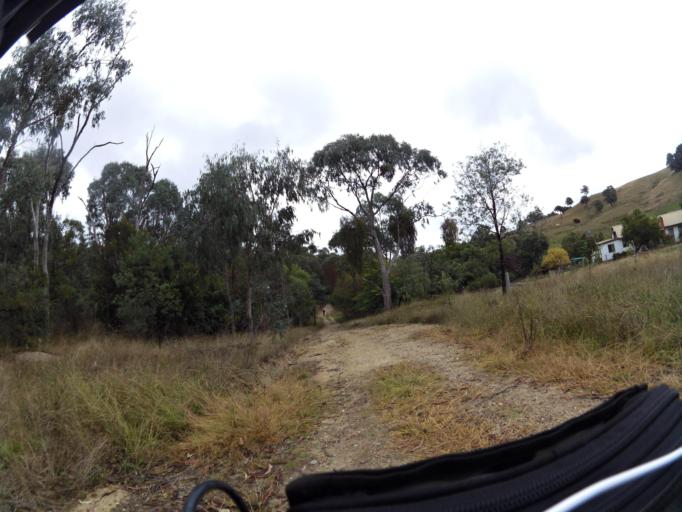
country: AU
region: New South Wales
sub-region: Greater Hume Shire
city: Holbrook
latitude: -36.1548
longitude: 147.4127
